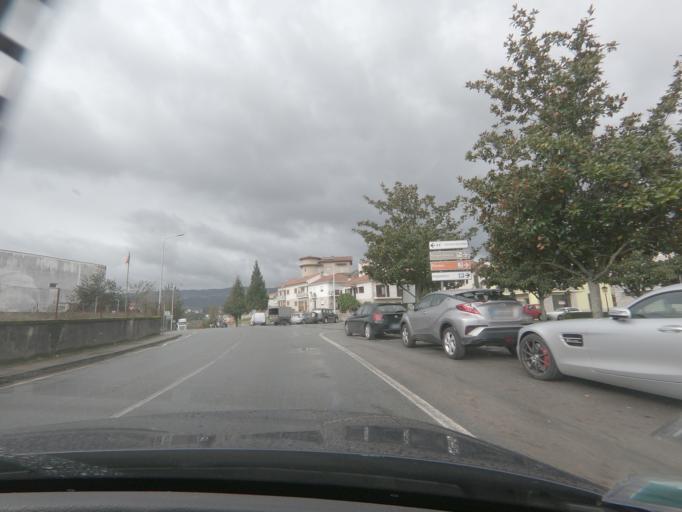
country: PT
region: Vila Real
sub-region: Mondim de Basto
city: Mondim de Basto
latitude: 41.4108
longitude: -7.9580
